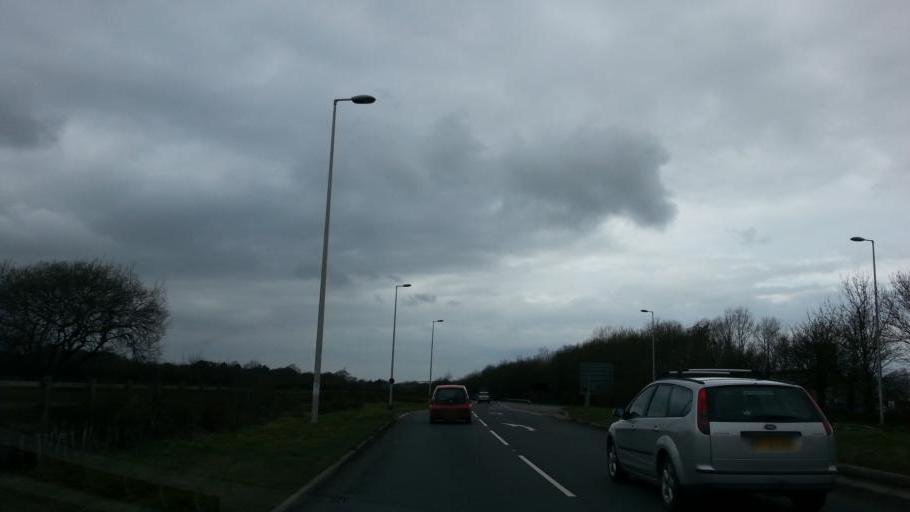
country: GB
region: England
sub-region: Devon
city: Barnstaple
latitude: 51.0623
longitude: -4.0833
